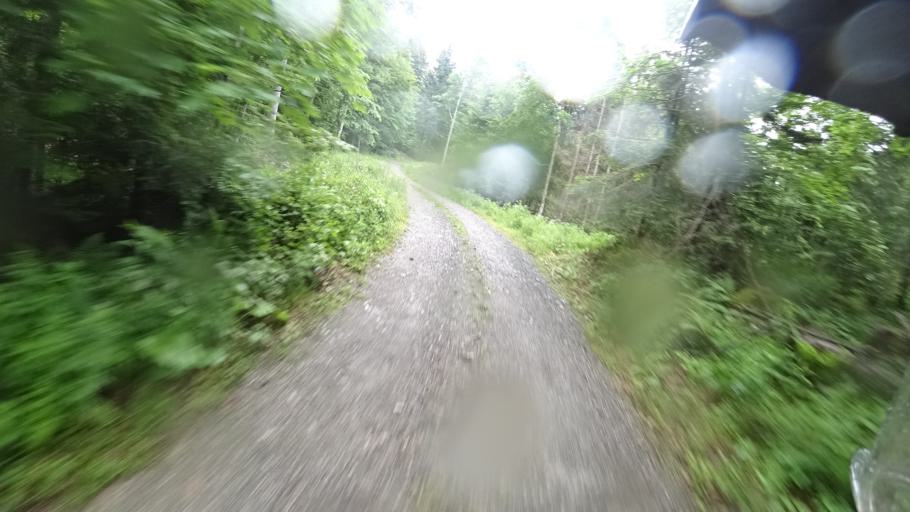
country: HR
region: Primorsko-Goranska
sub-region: Grad Delnice
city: Delnice
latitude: 45.3424
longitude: 14.9142
